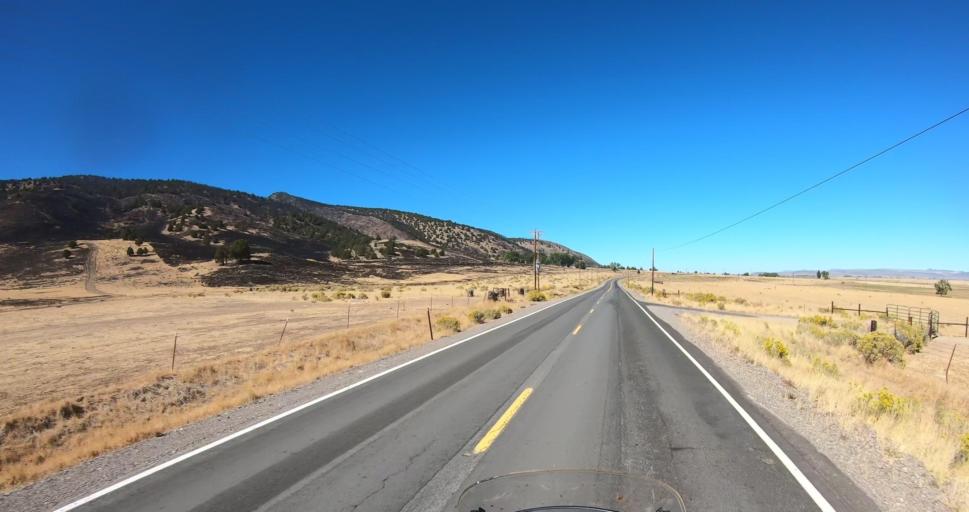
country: US
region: Oregon
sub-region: Lake County
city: Lakeview
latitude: 42.6352
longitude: -120.5174
